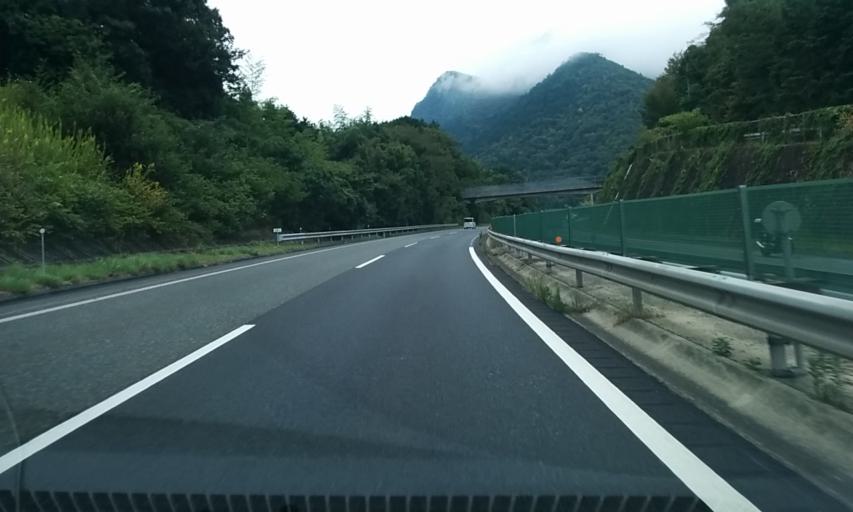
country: JP
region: Hyogo
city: Sasayama
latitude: 35.1403
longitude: 135.1354
